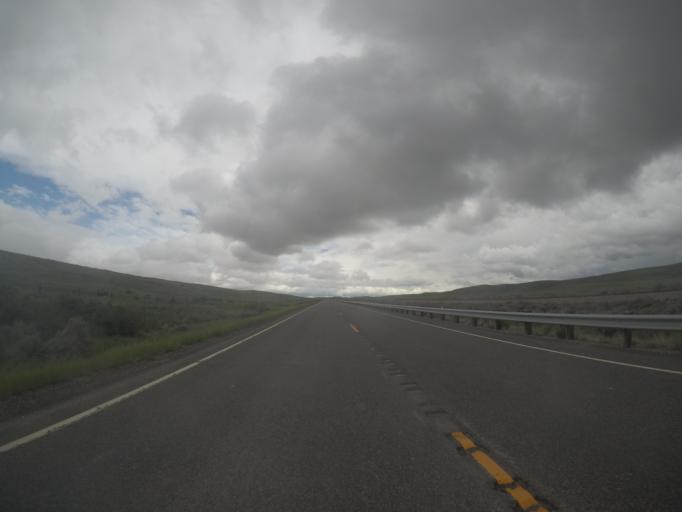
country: US
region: Wyoming
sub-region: Park County
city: Powell
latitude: 45.0904
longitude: -108.7160
